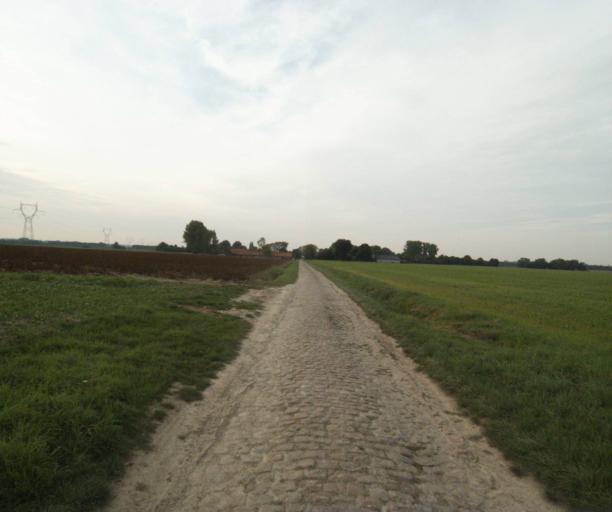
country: FR
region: Nord-Pas-de-Calais
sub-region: Departement du Nord
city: Phalempin
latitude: 50.5268
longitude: 3.0356
